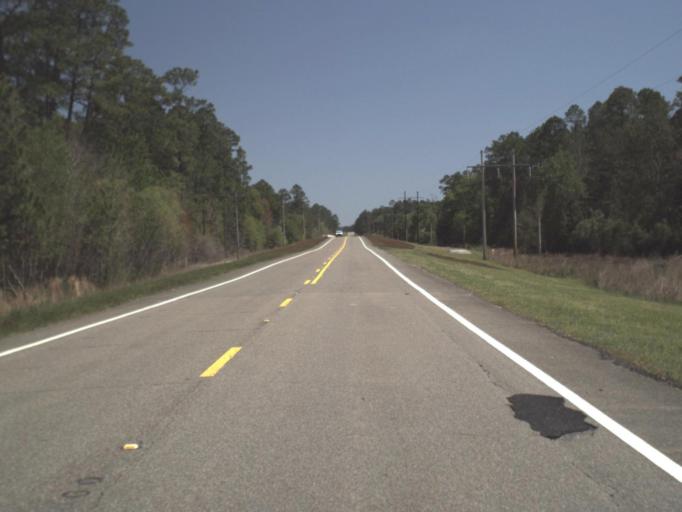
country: US
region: Florida
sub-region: Santa Rosa County
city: Point Baker
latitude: 30.8840
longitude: -86.9621
